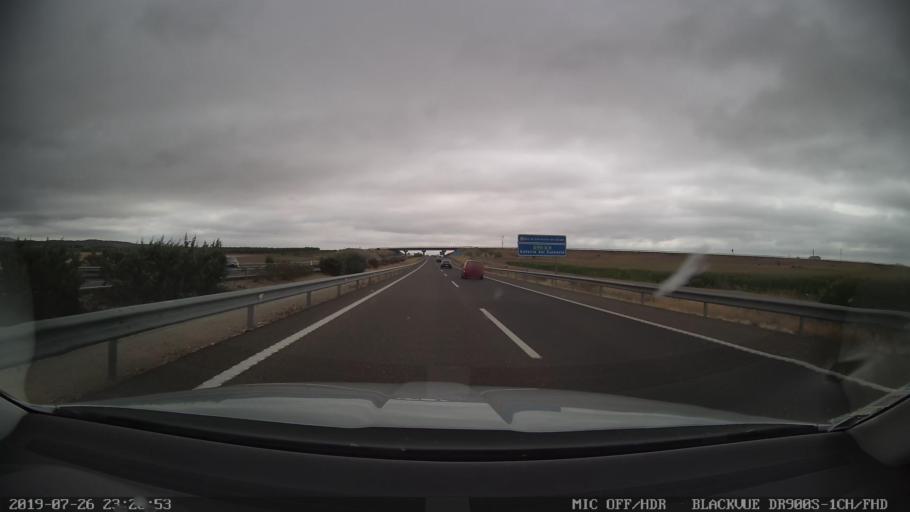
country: ES
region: Extremadura
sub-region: Provincia de Caceres
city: Miajadas
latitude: 39.1240
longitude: -5.9612
